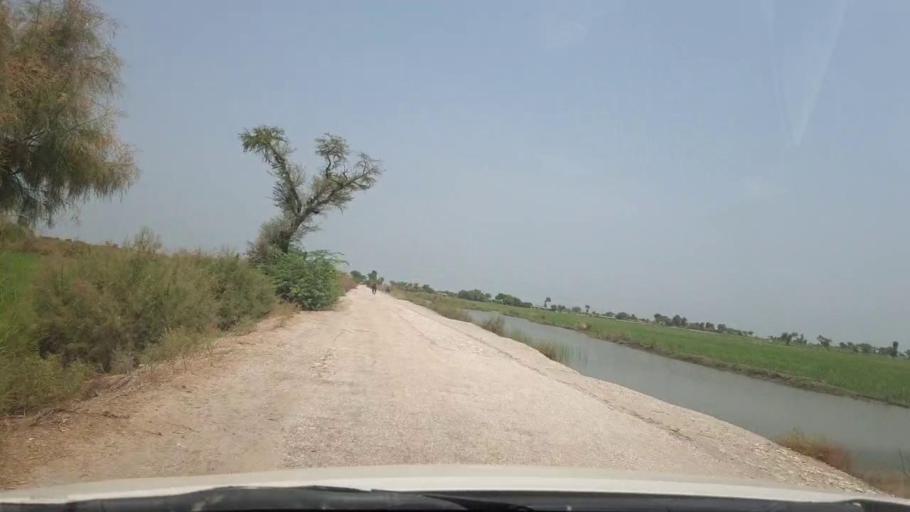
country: PK
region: Sindh
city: Rustam jo Goth
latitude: 28.0387
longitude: 68.8143
